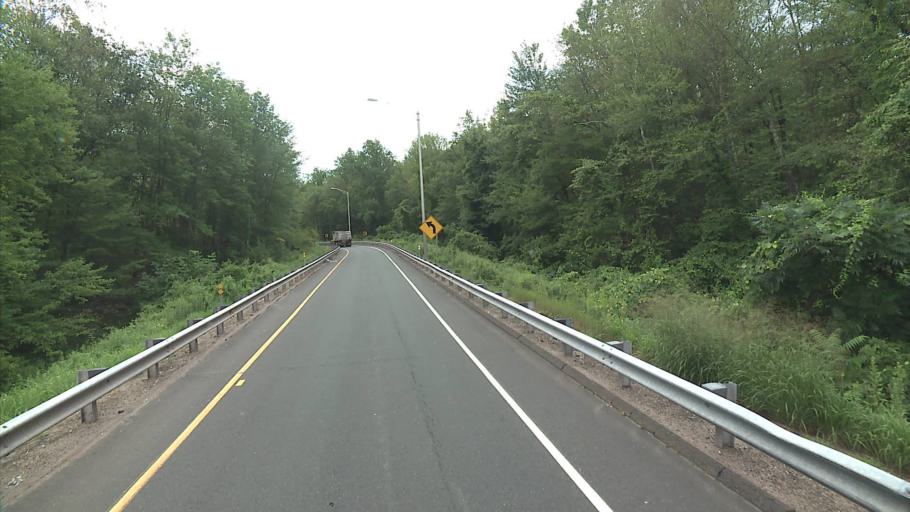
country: US
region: Connecticut
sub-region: Middlesex County
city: Higganum
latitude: 41.5142
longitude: -72.6011
